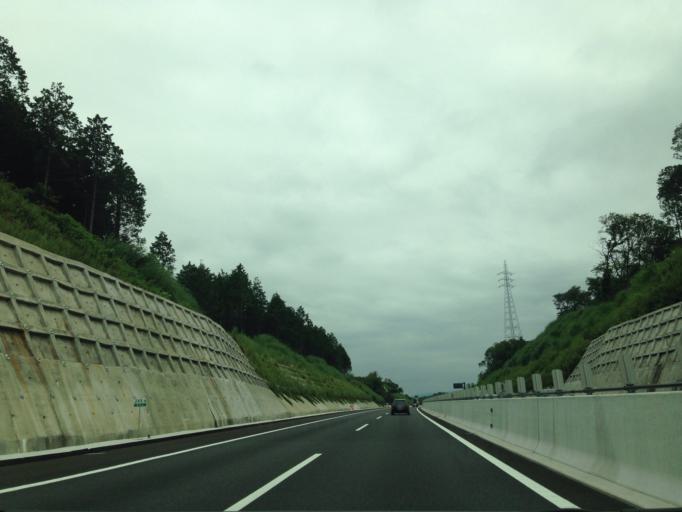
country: JP
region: Aichi
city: Okazaki
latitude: 34.9903
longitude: 137.2346
